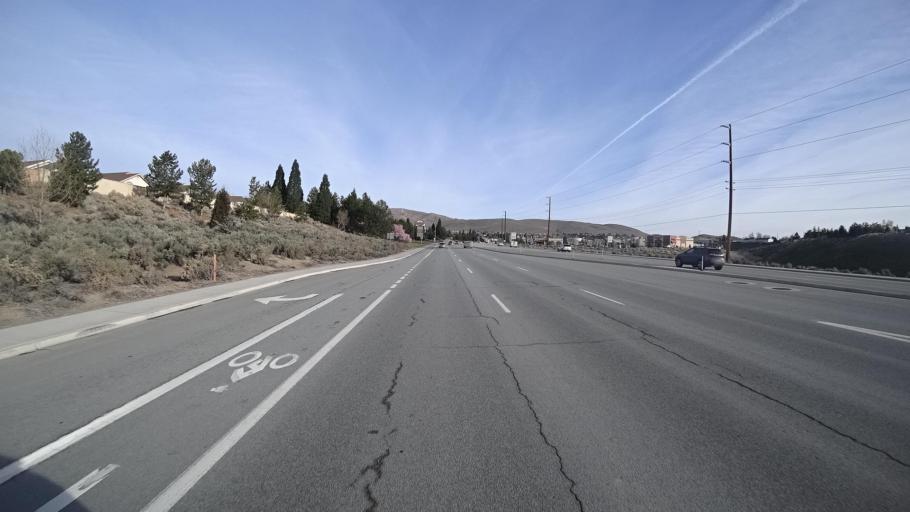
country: US
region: Nevada
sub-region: Washoe County
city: Reno
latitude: 39.5288
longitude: -119.8639
